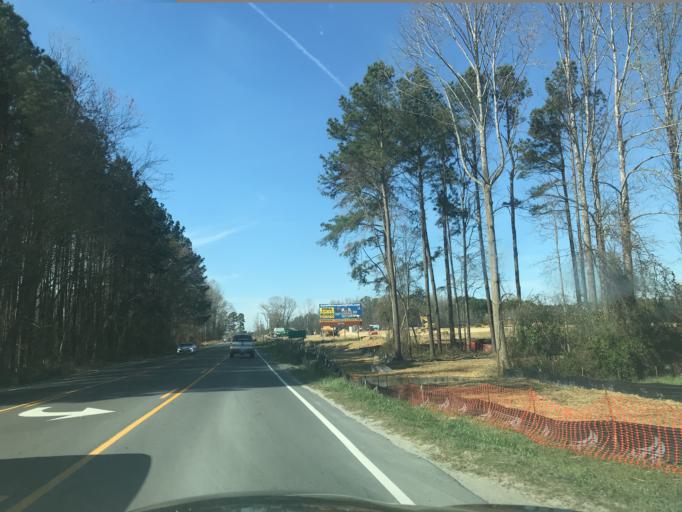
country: US
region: North Carolina
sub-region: Harnett County
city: Angier
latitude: 35.5318
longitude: -78.7450
